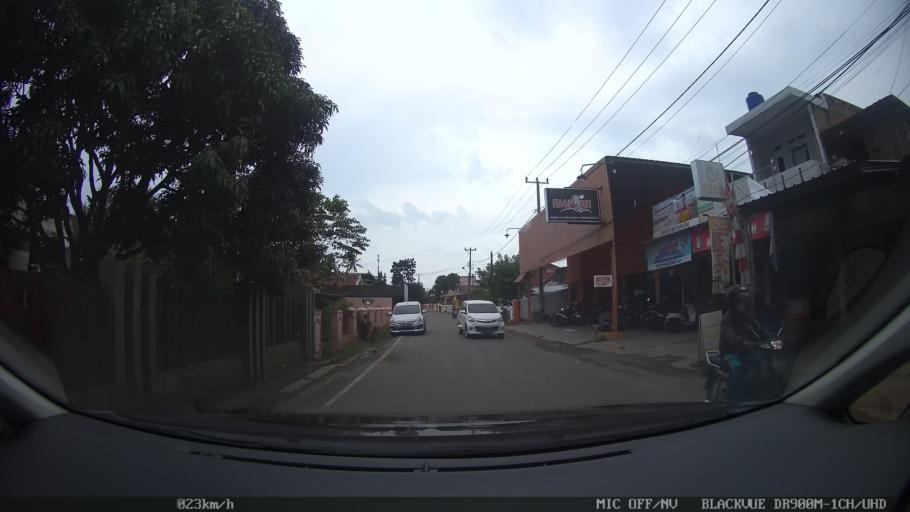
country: ID
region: Lampung
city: Kedaton
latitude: -5.3819
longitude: 105.2471
